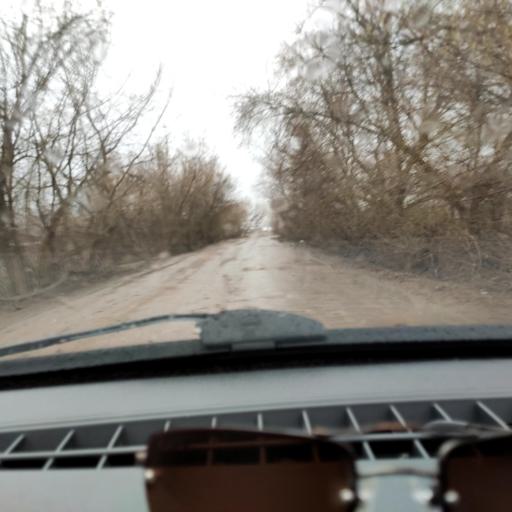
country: RU
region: Bashkortostan
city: Kabakovo
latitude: 54.5580
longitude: 56.0467
